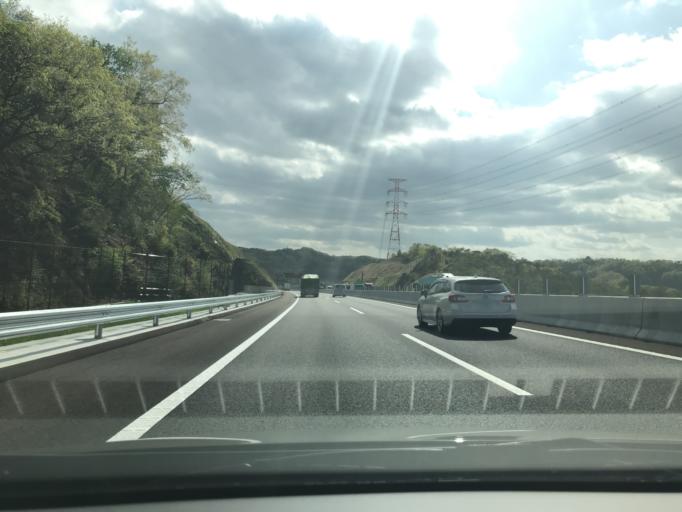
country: JP
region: Hyogo
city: Sandacho
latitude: 34.8614
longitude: 135.2565
